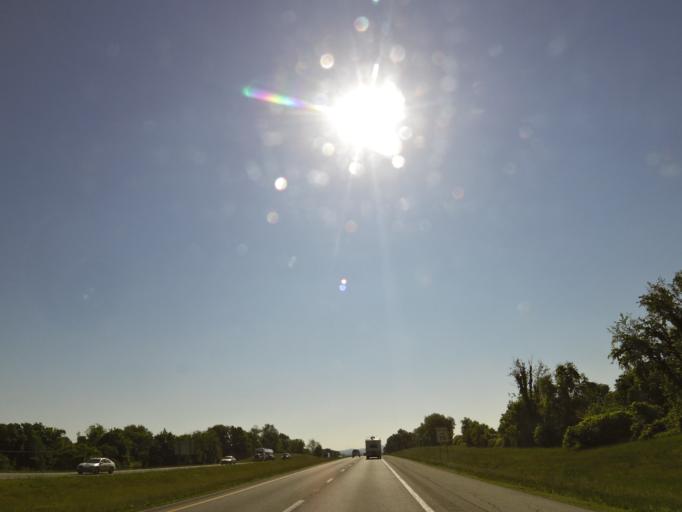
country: US
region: Kentucky
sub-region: Shelby County
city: Shelbyville
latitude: 38.1844
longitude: -85.2040
